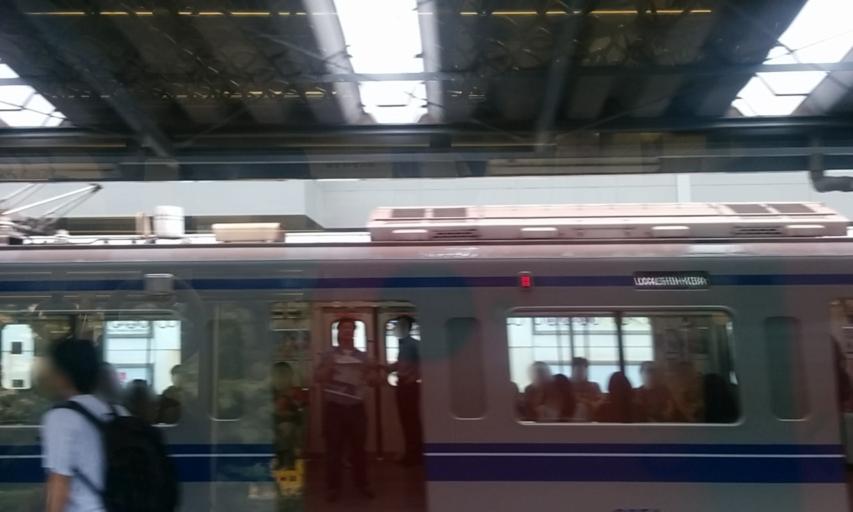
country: JP
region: Tokyo
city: Musashino
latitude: 35.7491
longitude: 139.5871
